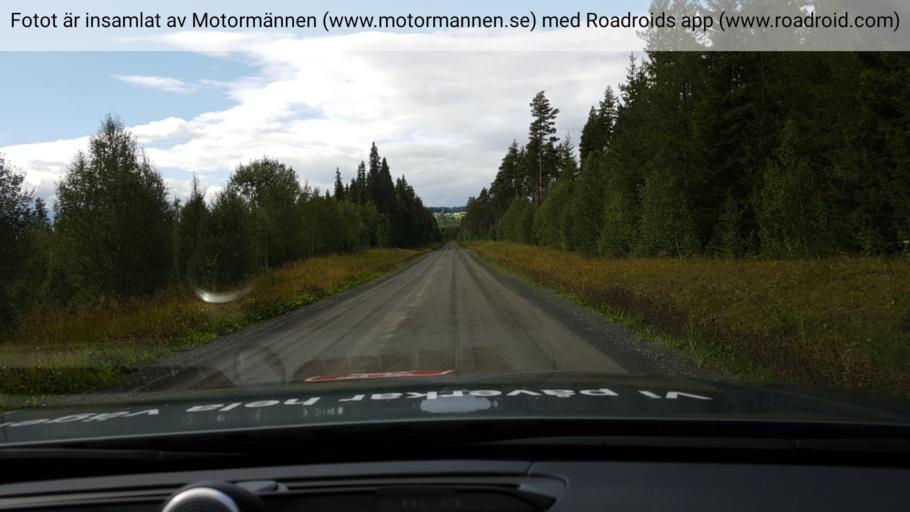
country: SE
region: Jaemtland
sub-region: OEstersunds Kommun
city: Lit
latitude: 63.6793
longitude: 14.7767
